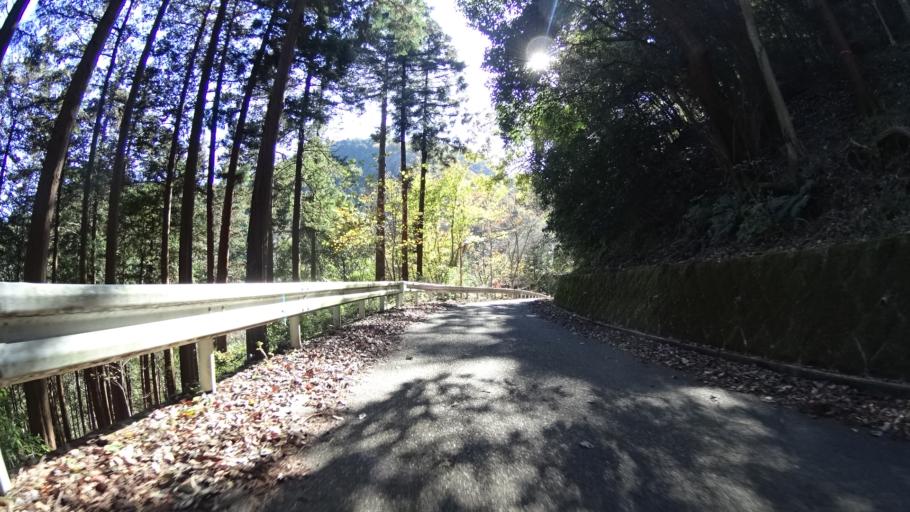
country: JP
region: Kanagawa
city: Atsugi
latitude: 35.5203
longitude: 139.2751
